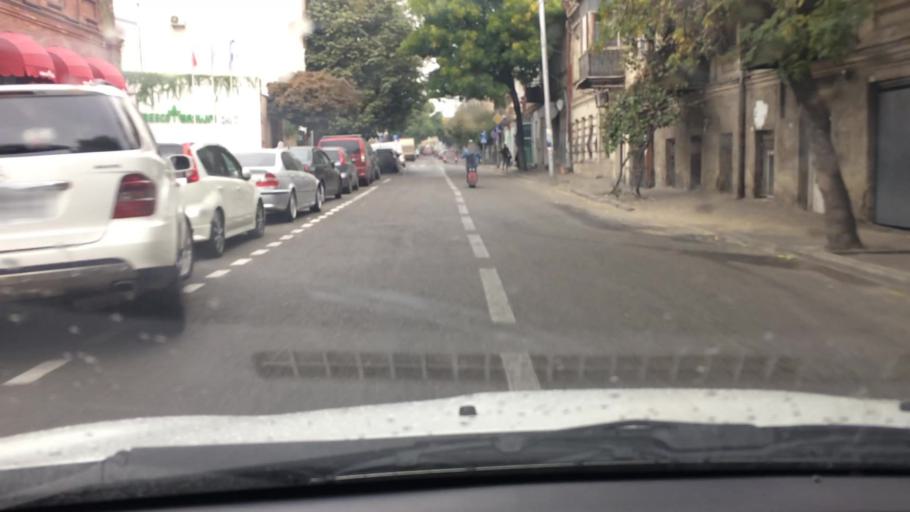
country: GE
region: T'bilisi
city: Tbilisi
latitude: 41.7076
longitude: 44.8052
